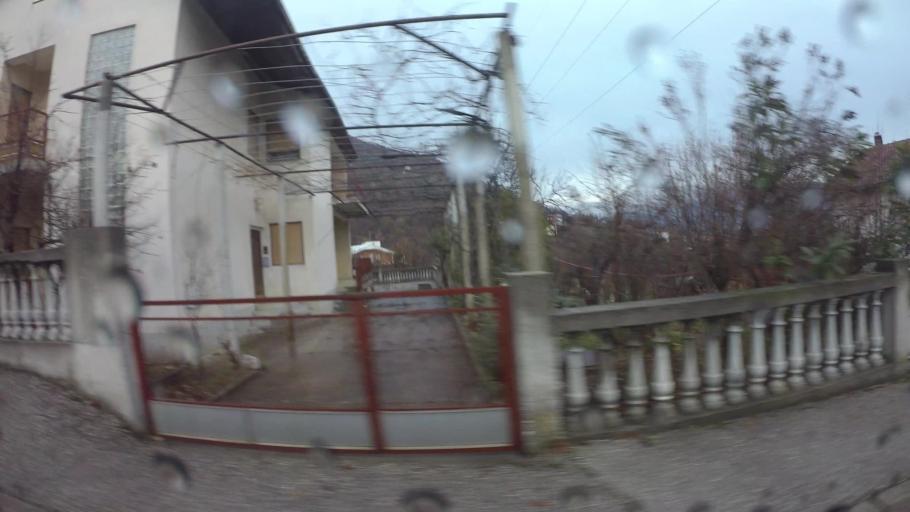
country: BA
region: Federation of Bosnia and Herzegovina
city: Cim
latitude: 43.3548
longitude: 17.7754
